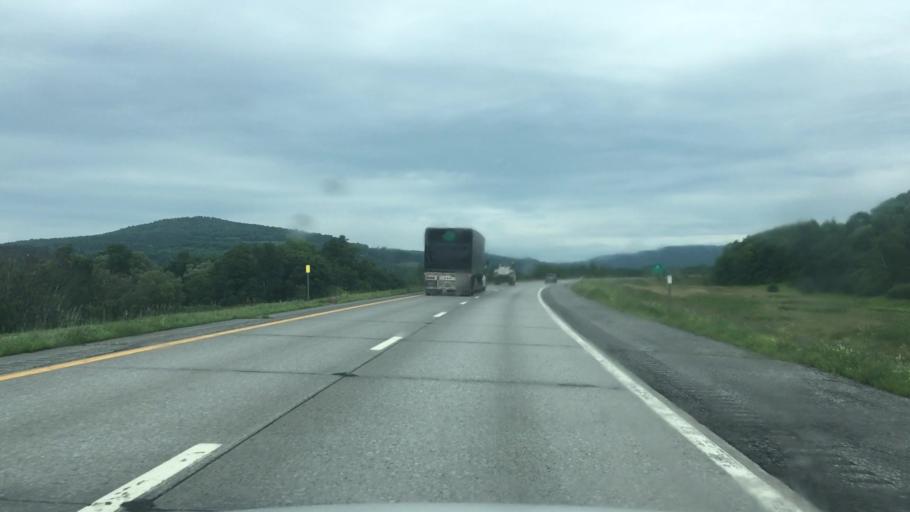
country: US
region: New York
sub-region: Otsego County
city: Worcester
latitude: 42.5845
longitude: -74.7574
